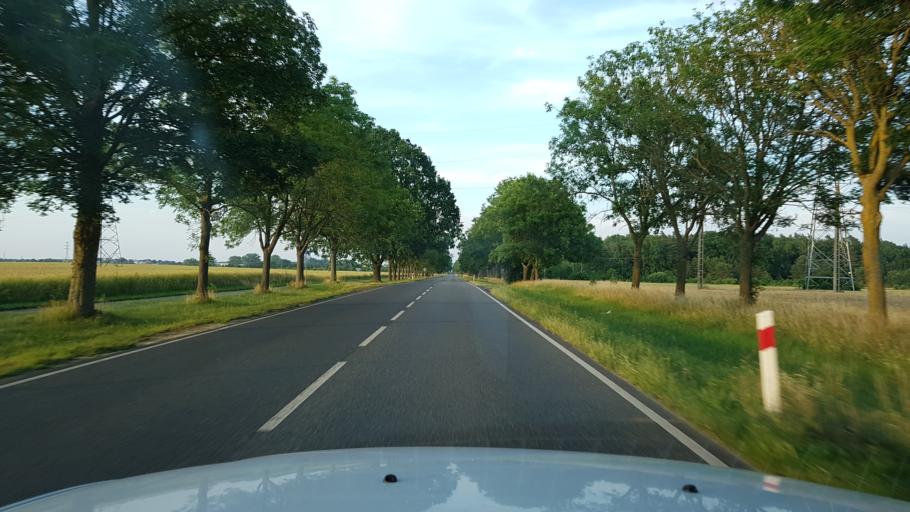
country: PL
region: West Pomeranian Voivodeship
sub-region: Powiat goleniowski
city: Nowogard
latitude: 53.6589
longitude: 15.0928
